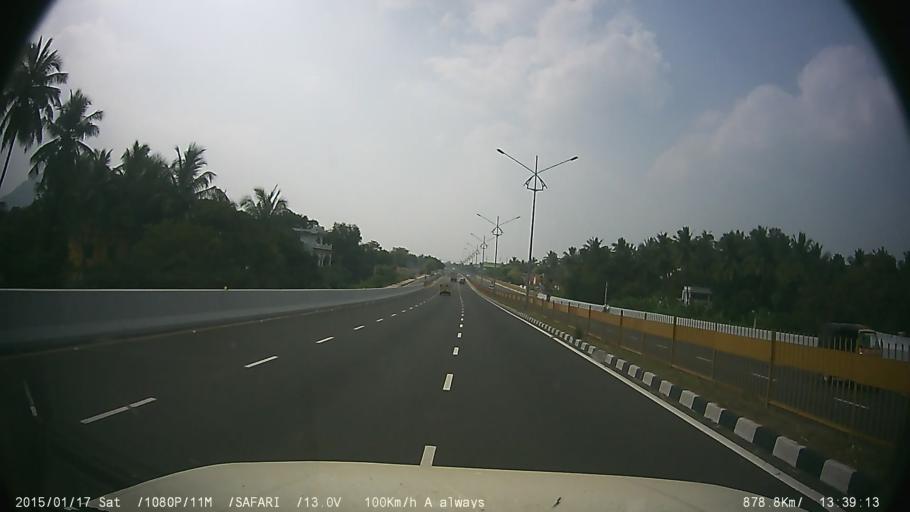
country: IN
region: Tamil Nadu
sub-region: Vellore
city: Katpadi
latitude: 12.9422
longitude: 79.1856
